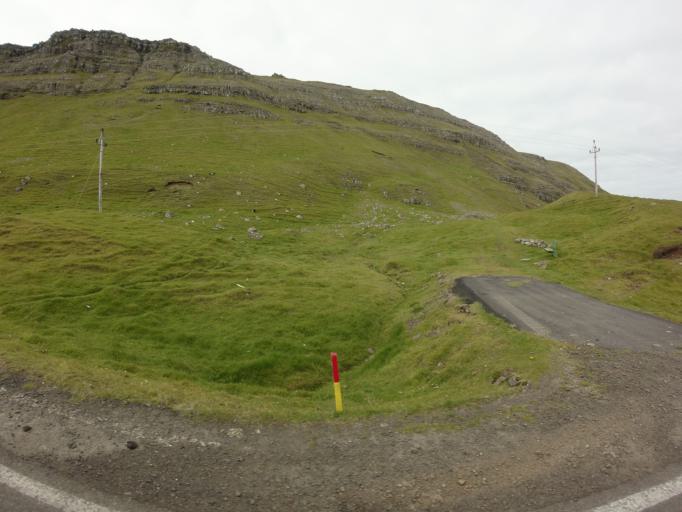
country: FO
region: Suduroy
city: Tvoroyri
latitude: 61.5888
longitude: -6.9469
